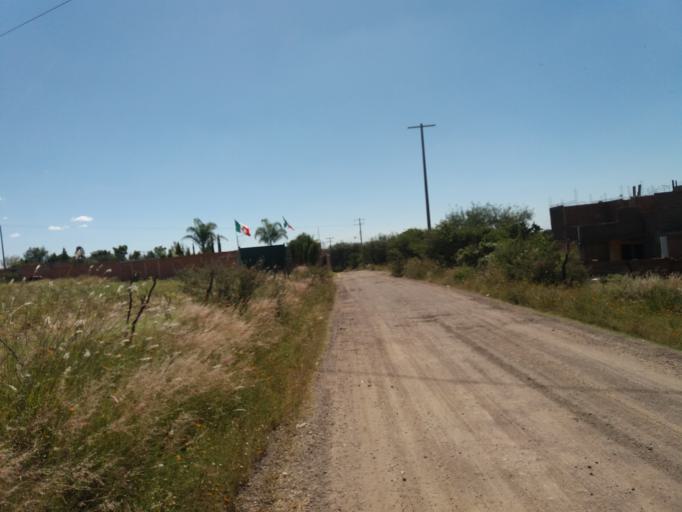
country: MX
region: Aguascalientes
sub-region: Aguascalientes
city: San Sebastian [Fraccionamiento]
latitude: 21.7823
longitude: -102.2280
